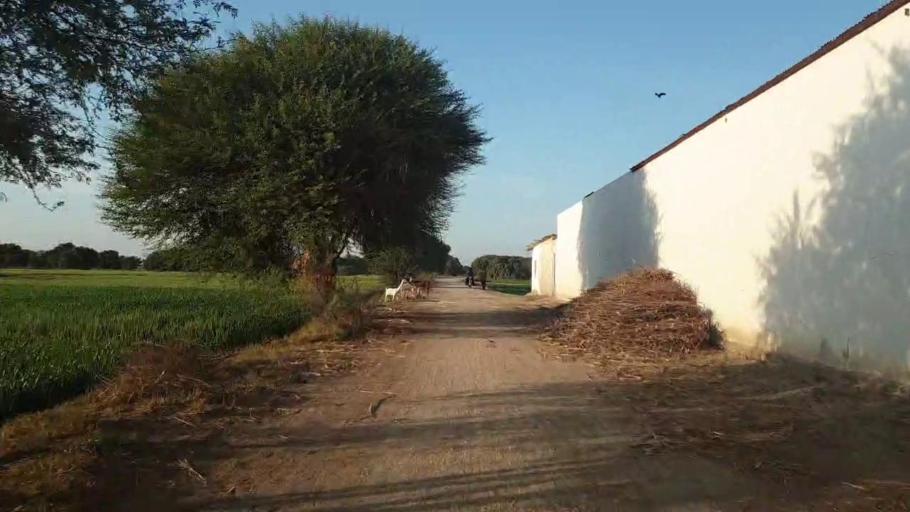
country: PK
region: Sindh
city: Chambar
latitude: 25.2727
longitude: 68.7726
